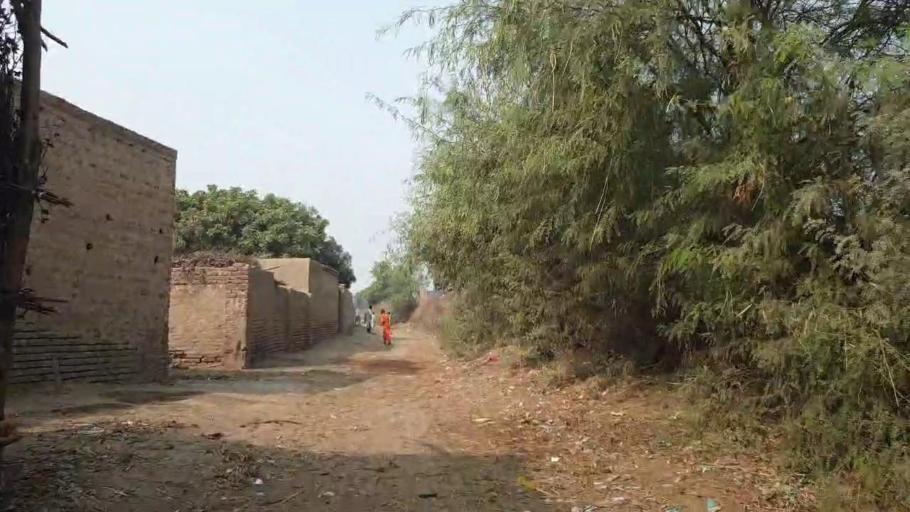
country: PK
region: Sindh
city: Tando Muhammad Khan
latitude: 25.2005
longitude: 68.5646
